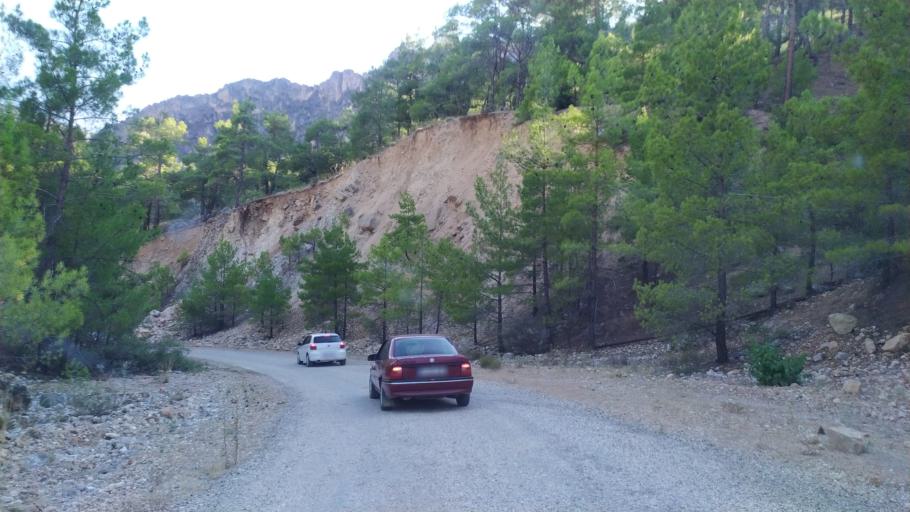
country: TR
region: Mersin
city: Mut
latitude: 36.5465
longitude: 33.2336
